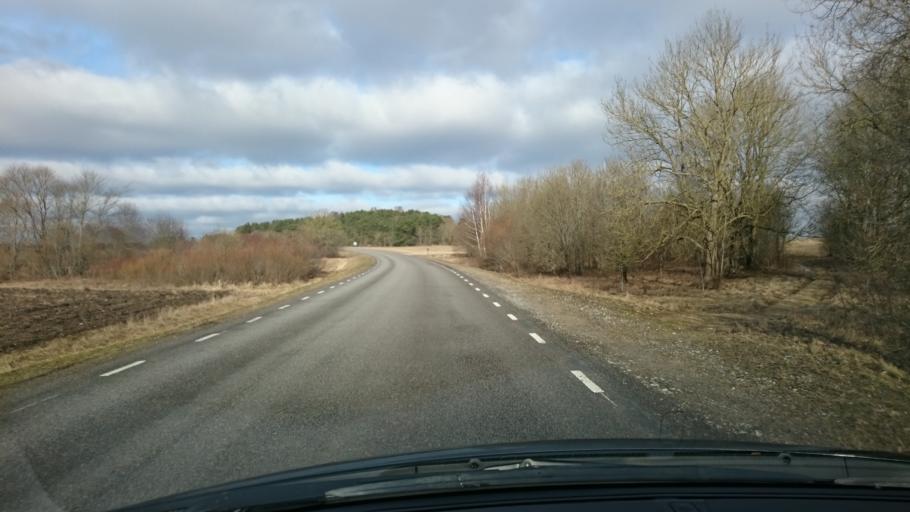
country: EE
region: Harju
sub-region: Keila linn
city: Keila
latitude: 59.3381
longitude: 24.3715
